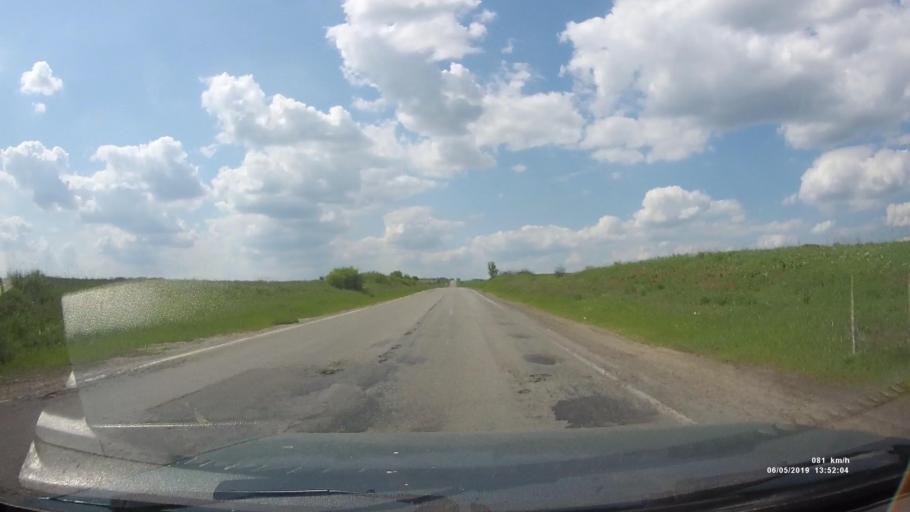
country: RU
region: Rostov
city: Melikhovskaya
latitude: 47.6600
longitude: 40.4823
